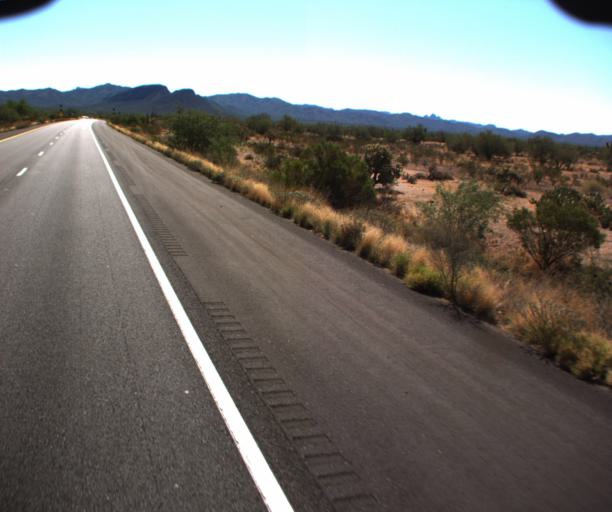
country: US
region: Arizona
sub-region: Pinal County
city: Gold Camp
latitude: 33.2575
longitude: -111.3098
